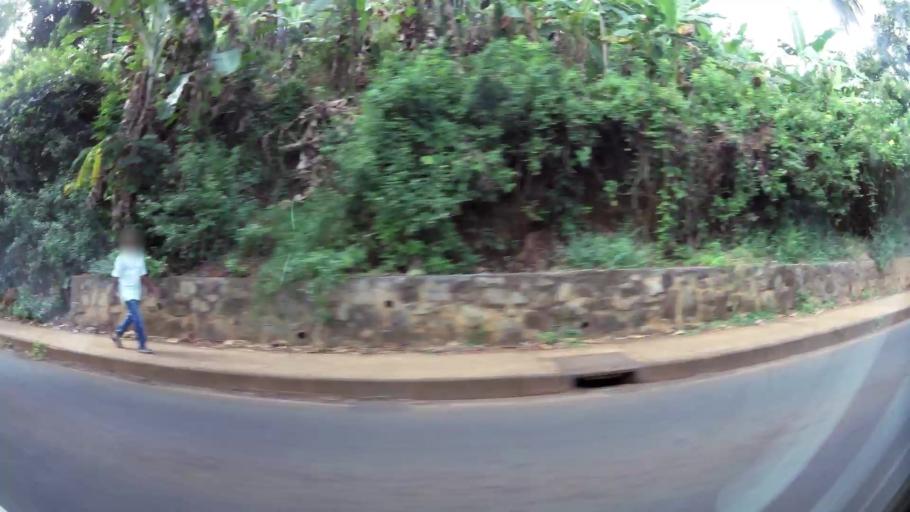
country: YT
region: Chiconi
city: Chiconi
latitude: -12.8422
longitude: 45.1170
